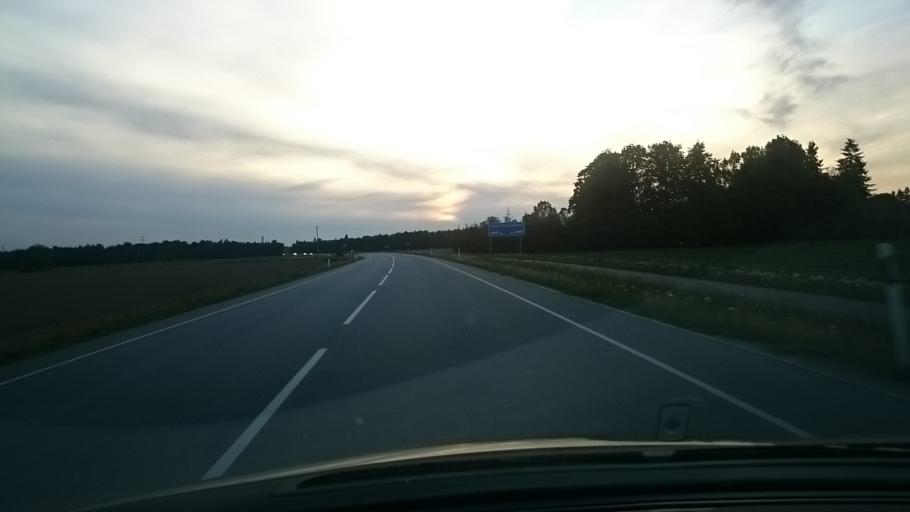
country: EE
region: Jaervamaa
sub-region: Paide linn
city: Paide
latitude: 58.7601
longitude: 25.5533
